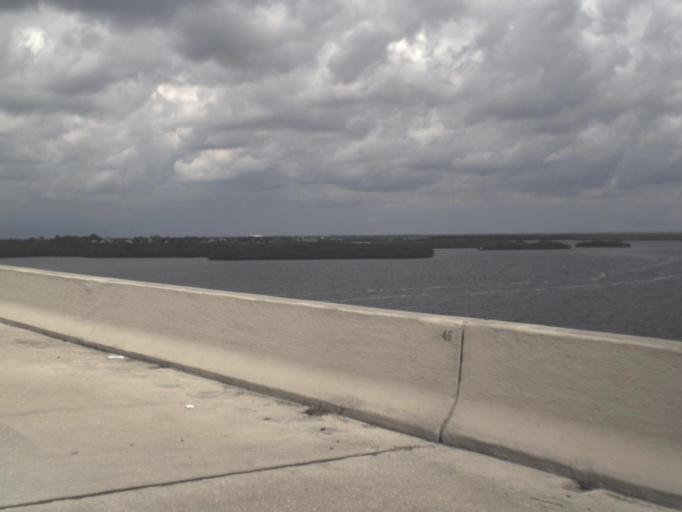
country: US
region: Florida
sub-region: Charlotte County
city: Cleveland
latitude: 26.9582
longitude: -82.0201
